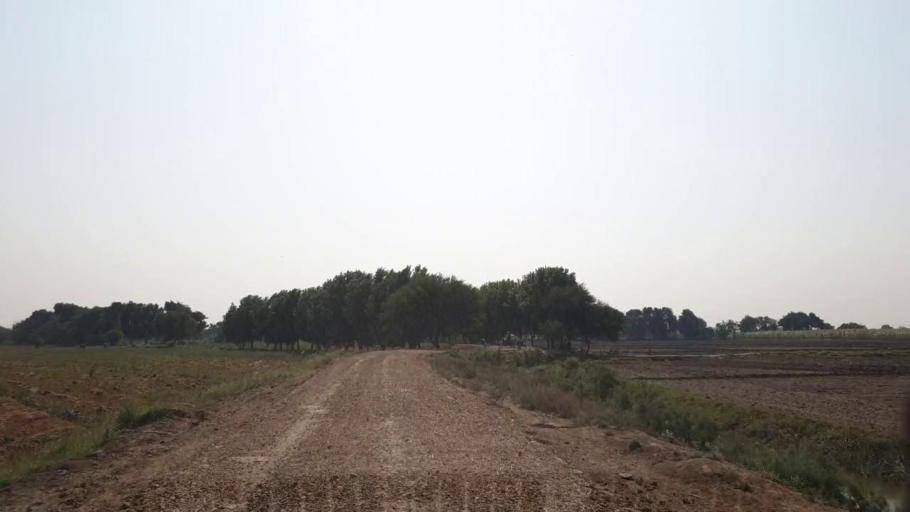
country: PK
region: Sindh
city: Tando Muhammad Khan
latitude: 25.0176
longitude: 68.4178
